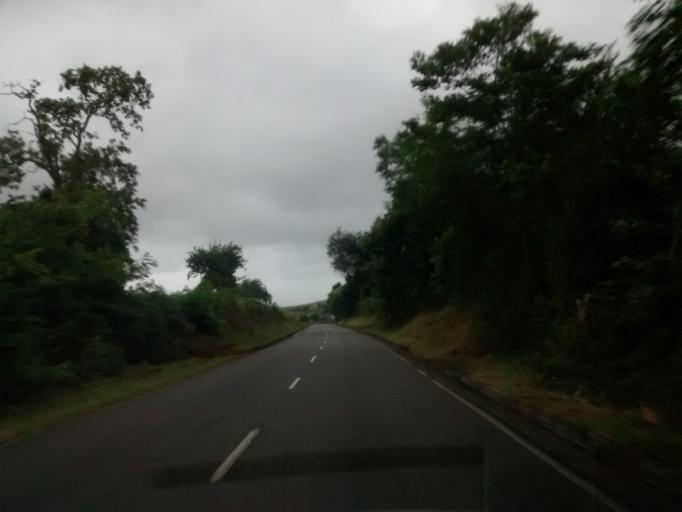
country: ES
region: Asturias
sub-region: Province of Asturias
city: Villaviciosa
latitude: 43.5049
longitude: -5.4241
